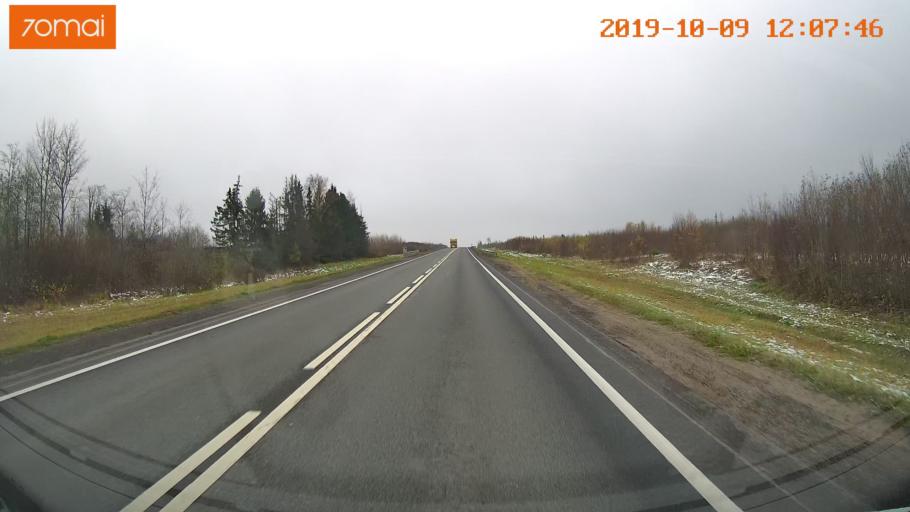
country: RU
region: Jaroslavl
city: Prechistoye
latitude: 58.5952
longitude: 40.3438
